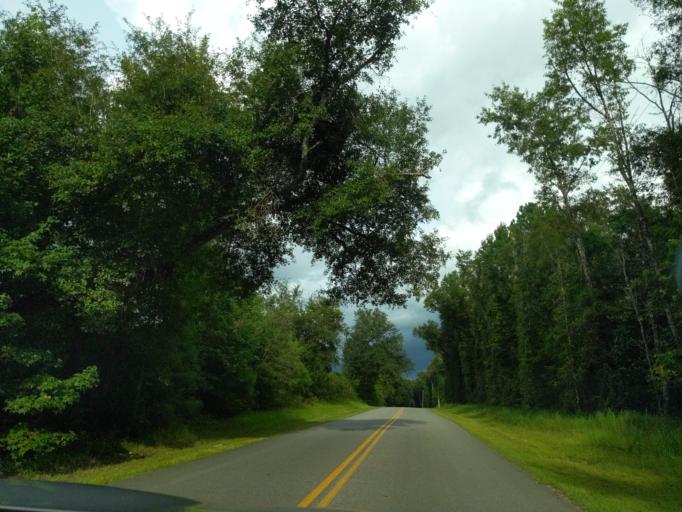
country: US
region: Florida
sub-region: Jefferson County
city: Monticello
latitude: 30.4782
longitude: -83.8929
